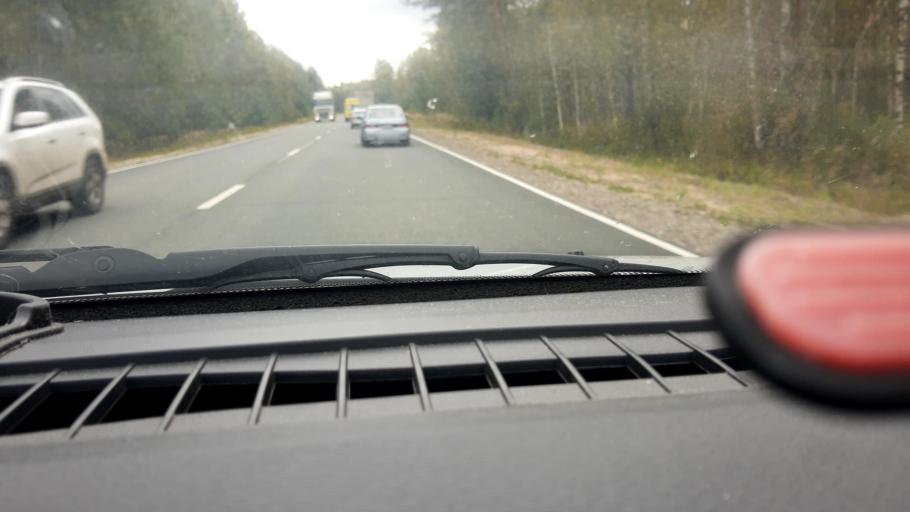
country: RU
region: Nizjnij Novgorod
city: Uren'
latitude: 57.3922
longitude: 45.6870
